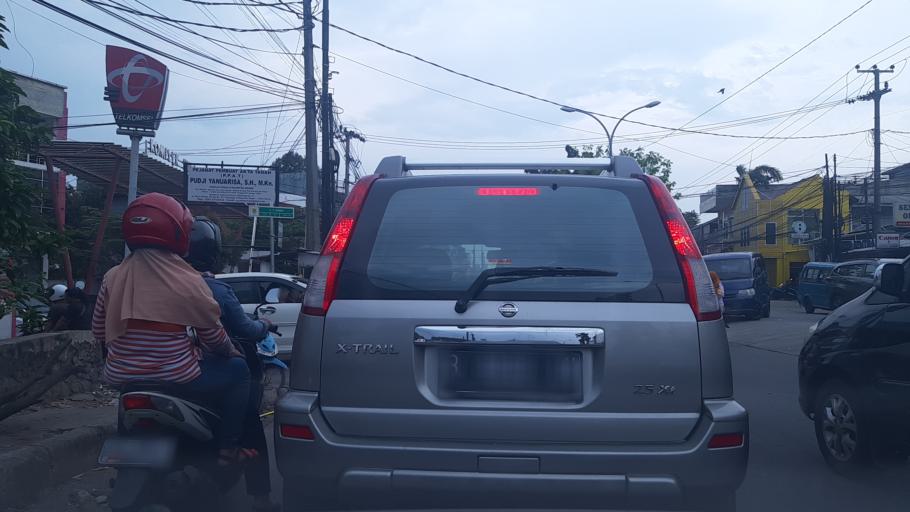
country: ID
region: West Java
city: Cibinong
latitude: -6.4694
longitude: 106.8599
